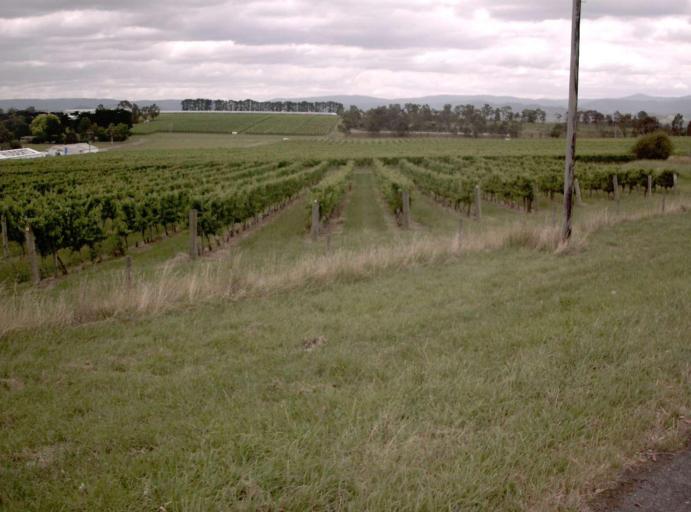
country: AU
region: Victoria
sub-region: Yarra Ranges
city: Yarra Glen
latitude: -37.7009
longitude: 145.4165
